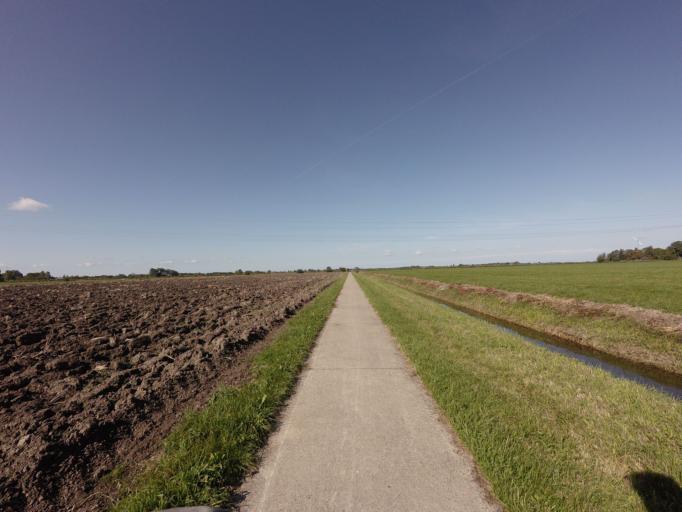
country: NL
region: Friesland
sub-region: Gemeente Leeuwarden
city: Wirdum
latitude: 53.1531
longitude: 5.7688
